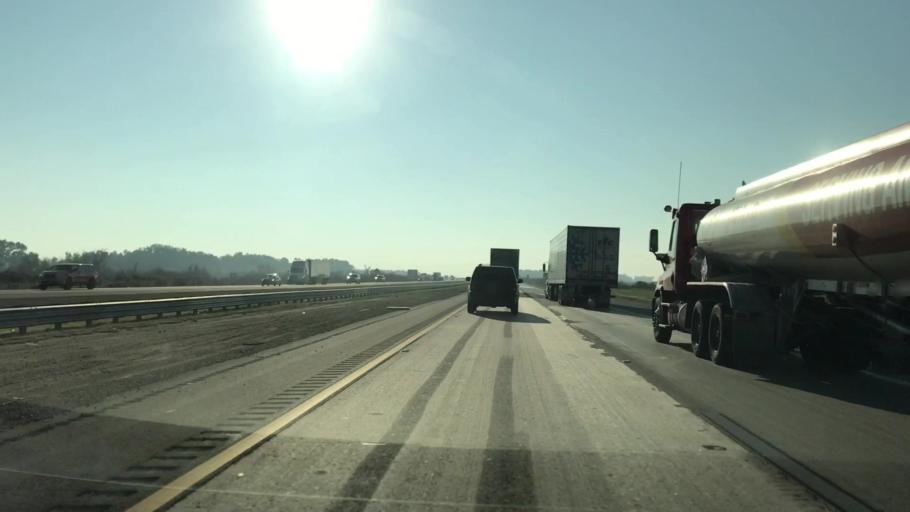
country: US
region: California
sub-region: Kern County
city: Lost Hills
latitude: 35.6123
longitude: -119.6490
